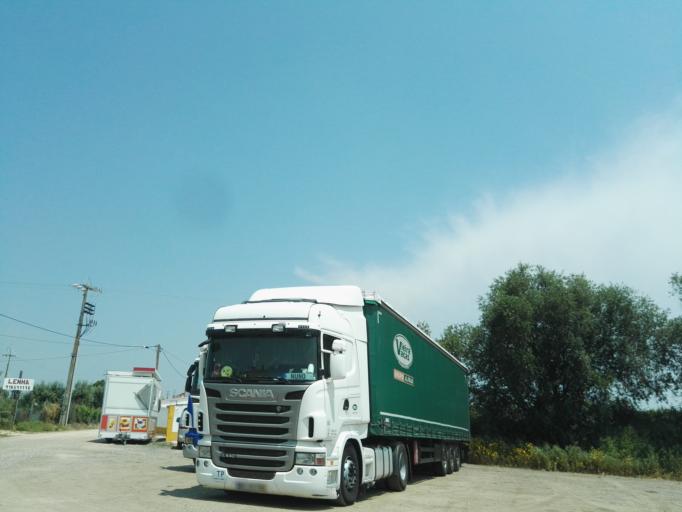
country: PT
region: Santarem
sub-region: Golega
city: Golega
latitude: 39.4067
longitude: -8.4765
